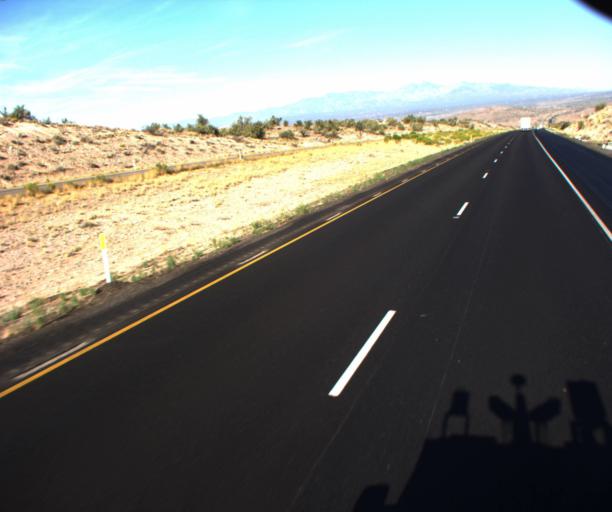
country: US
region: Arizona
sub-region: Mohave County
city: Peach Springs
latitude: 35.1606
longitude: -113.6096
